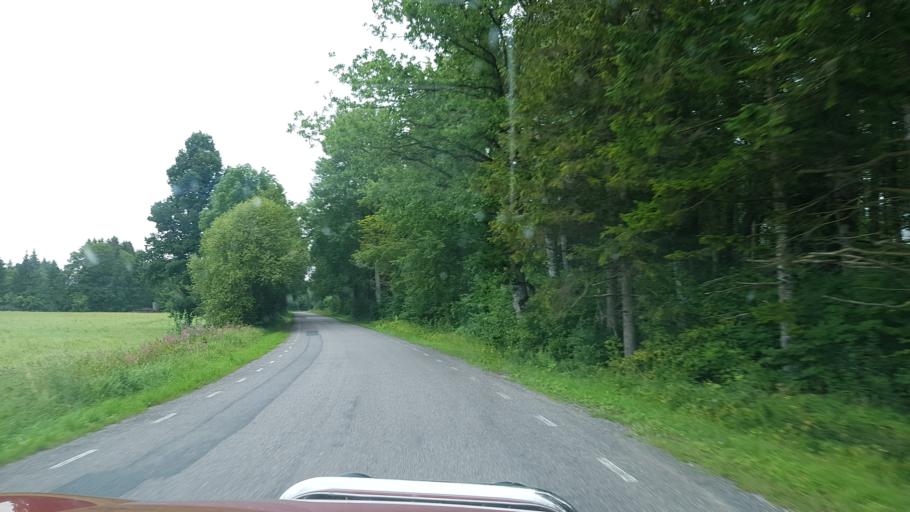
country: EE
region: Laeaene
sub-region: Lihula vald
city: Lihula
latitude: 58.8753
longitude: 23.8059
